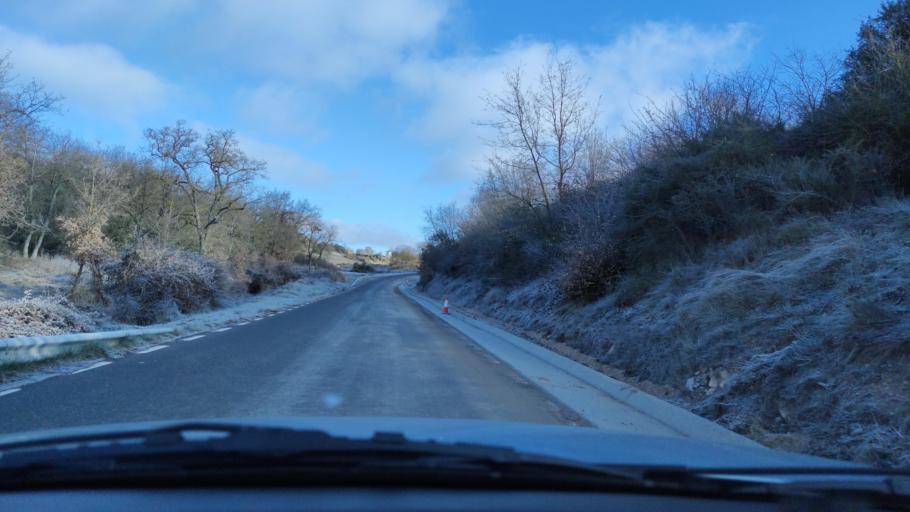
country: ES
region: Catalonia
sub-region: Provincia de Barcelona
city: Pujalt
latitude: 41.7114
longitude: 1.3517
